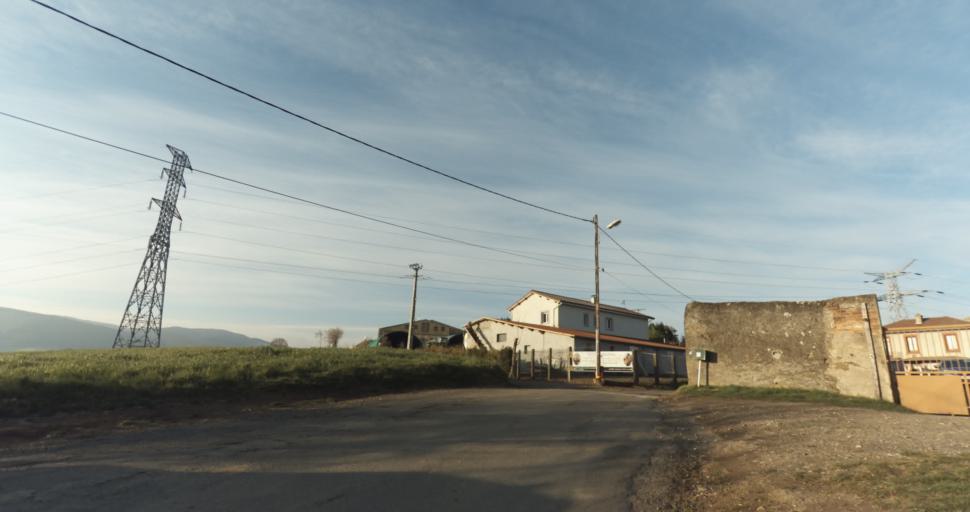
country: FR
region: Rhone-Alpes
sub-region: Departement de la Loire
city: Saint-Jean-Bonnefonds
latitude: 45.4570
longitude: 4.4408
